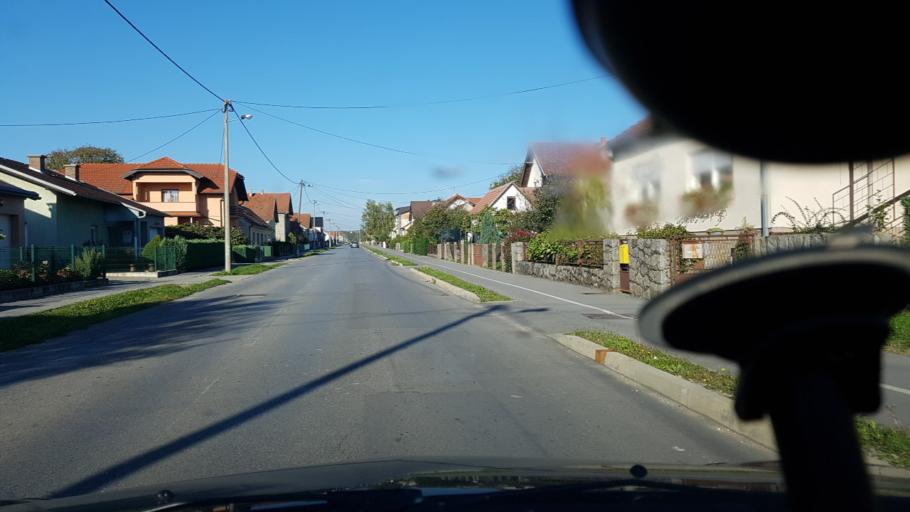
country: HR
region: Bjelovarsko-Bilogorska
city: Bjelovar
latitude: 45.9141
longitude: 16.8560
